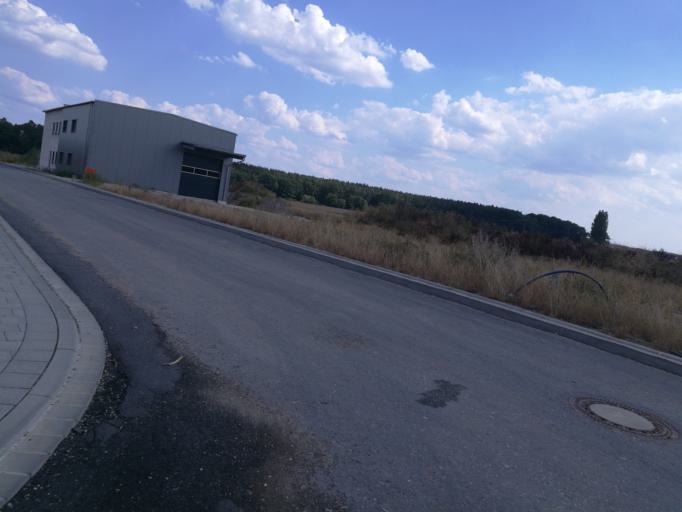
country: DE
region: Bavaria
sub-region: Regierungsbezirk Mittelfranken
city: Veitsbronn
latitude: 49.5019
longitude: 10.8811
